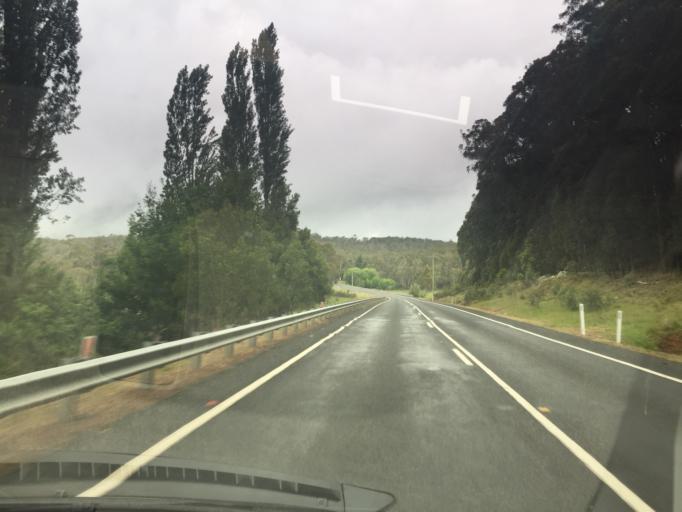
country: AU
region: New South Wales
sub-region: Bombala
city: Bombala
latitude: -36.6064
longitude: 149.3557
